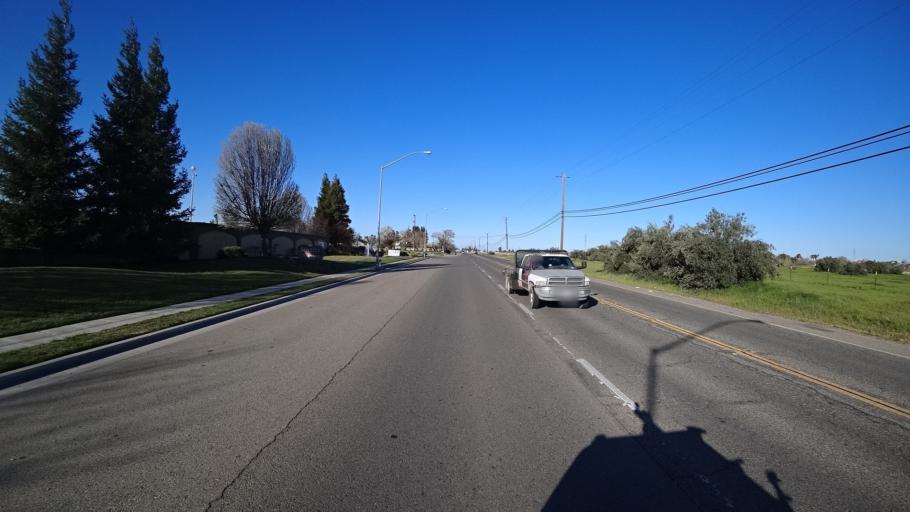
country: US
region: California
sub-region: Fresno County
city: West Park
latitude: 36.8080
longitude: -119.8929
